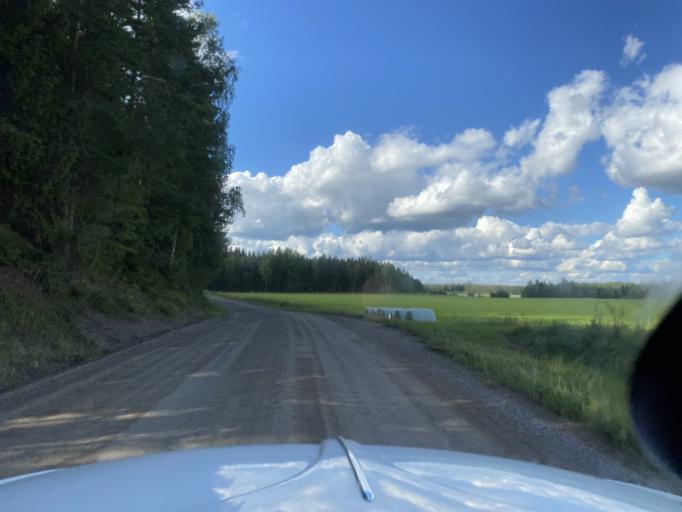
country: FI
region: Pirkanmaa
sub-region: Lounais-Pirkanmaa
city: Punkalaidun
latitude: 61.1164
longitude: 23.2729
